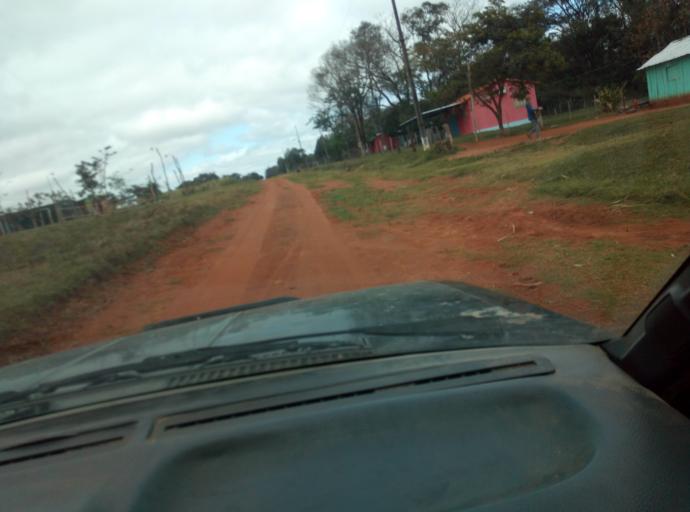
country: PY
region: Caaguazu
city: Doctor Cecilio Baez
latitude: -25.1491
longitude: -56.2906
